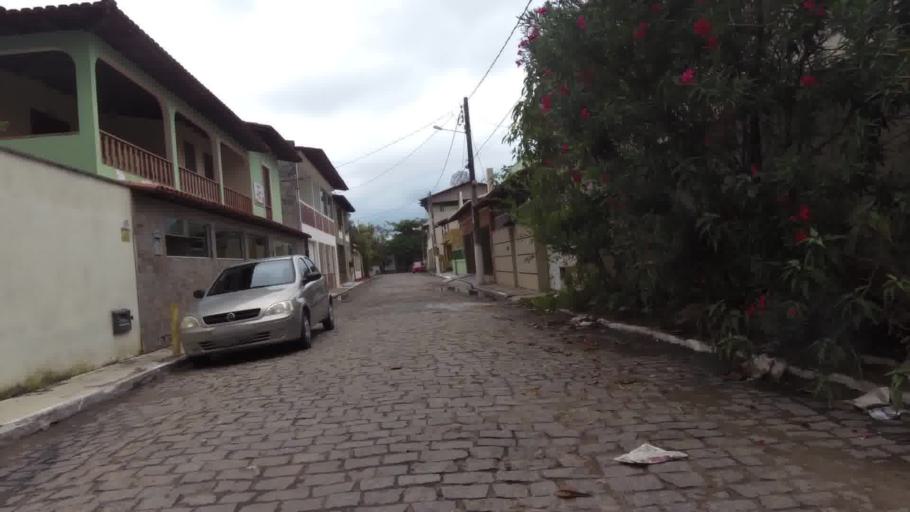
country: BR
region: Espirito Santo
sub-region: Marataizes
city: Marataizes
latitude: -21.0424
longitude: -40.8289
